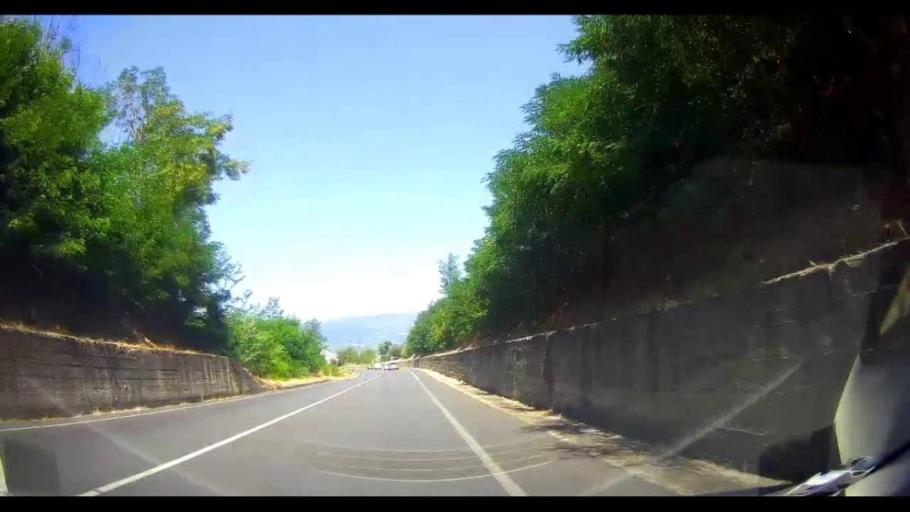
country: IT
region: Calabria
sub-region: Provincia di Cosenza
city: Zumpano
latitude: 39.2987
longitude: 16.2924
